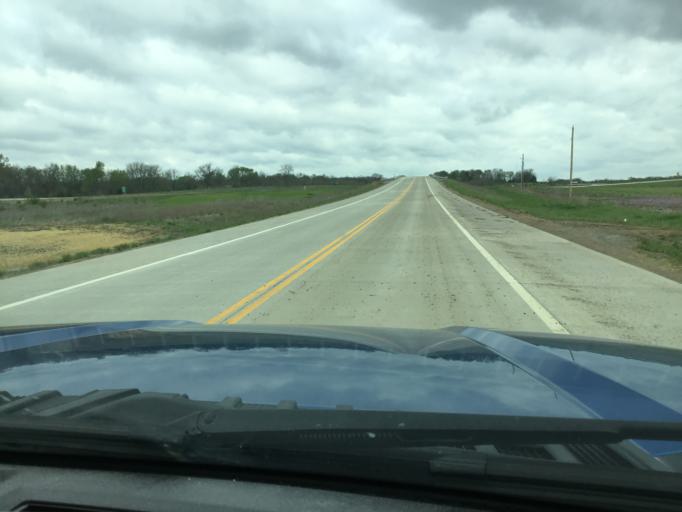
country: US
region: Kansas
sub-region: Douglas County
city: Lawrence
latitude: 38.9288
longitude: -95.1768
